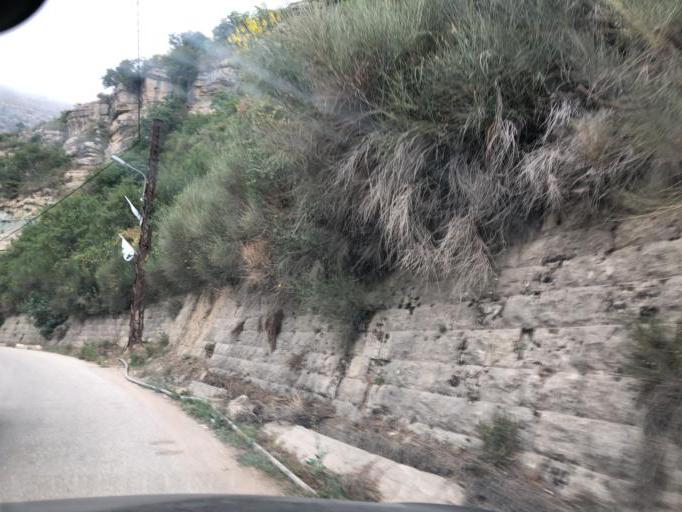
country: LB
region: Liban-Nord
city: Bcharre
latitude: 34.1160
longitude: 35.9073
